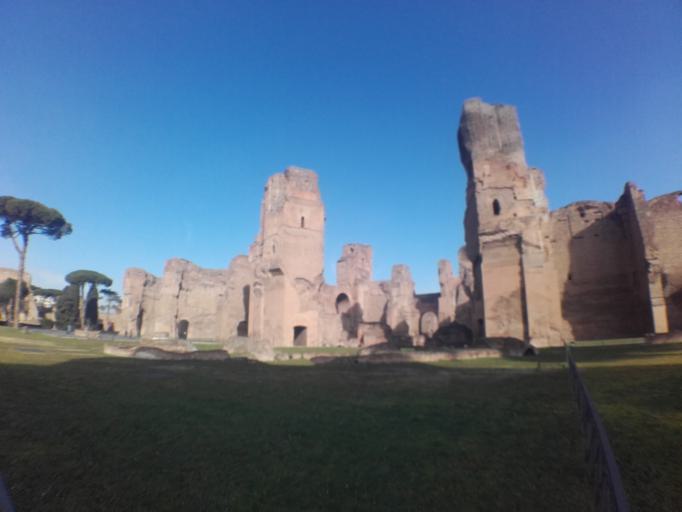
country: IT
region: Latium
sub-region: Citta metropolitana di Roma Capitale
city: Rome
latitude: 41.8786
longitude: 12.4925
